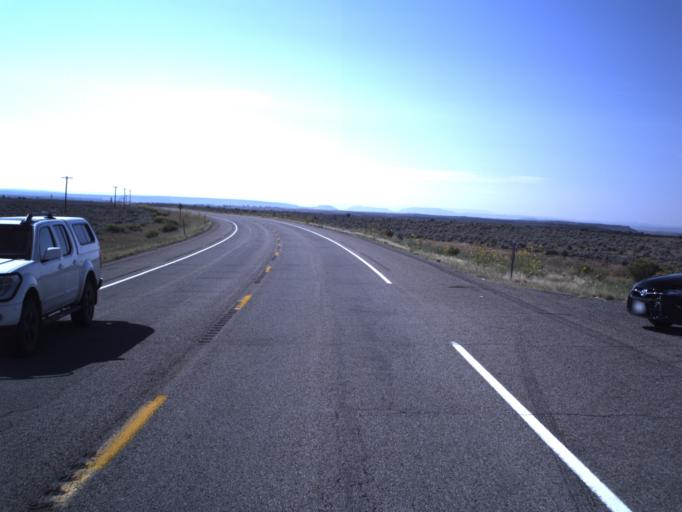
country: US
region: Utah
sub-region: San Juan County
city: Blanding
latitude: 37.5142
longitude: -109.4938
